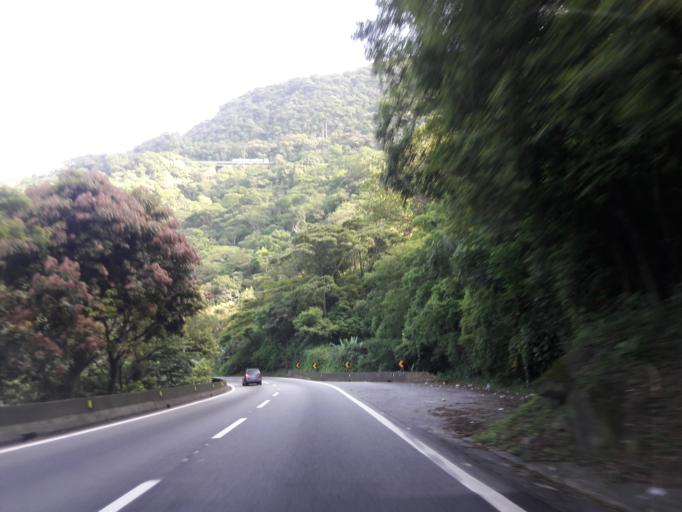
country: BR
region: Sao Paulo
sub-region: Cubatao
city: Cubatao
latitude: -23.8906
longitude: -46.4848
